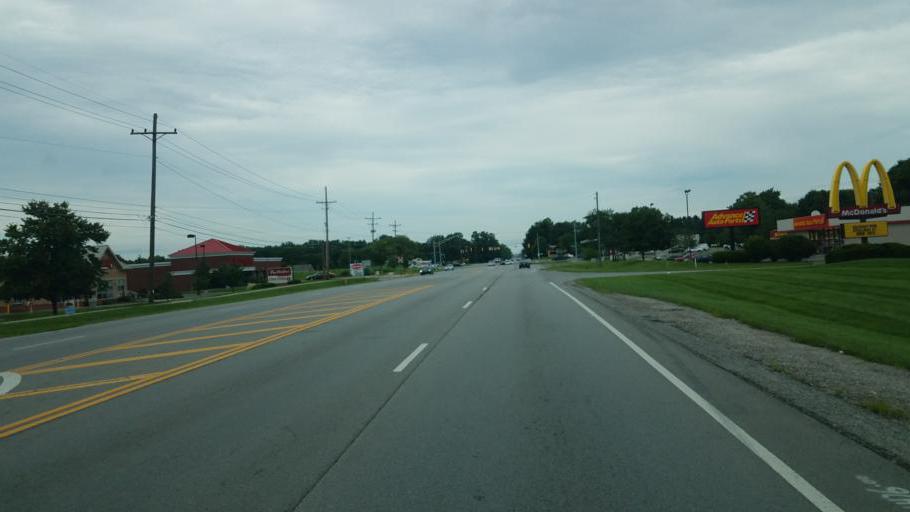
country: US
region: Ohio
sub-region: Franklin County
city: Groveport
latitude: 39.8976
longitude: -82.8822
